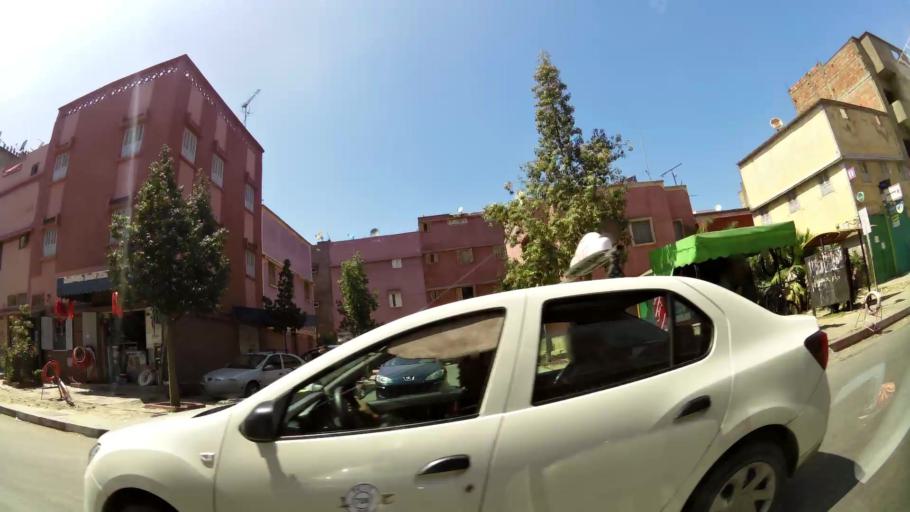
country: MA
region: Gharb-Chrarda-Beni Hssen
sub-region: Kenitra Province
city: Kenitra
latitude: 34.2454
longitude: -6.5479
